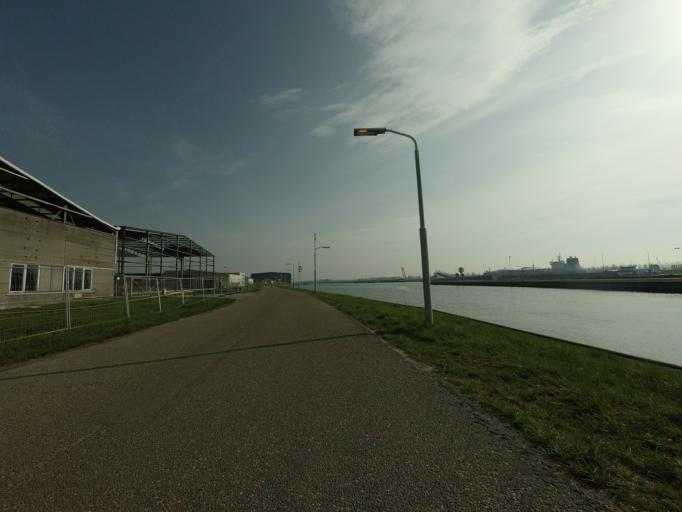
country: NL
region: Zeeland
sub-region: Gemeente Terneuzen
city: Terneuzen
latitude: 51.3324
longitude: 3.8209
